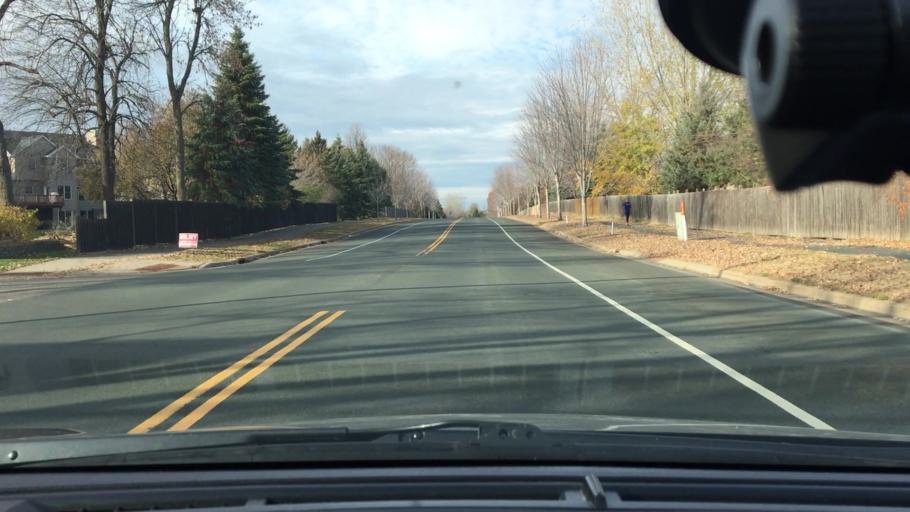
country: US
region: Minnesota
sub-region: Hennepin County
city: Corcoran
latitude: 45.1166
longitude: -93.5069
